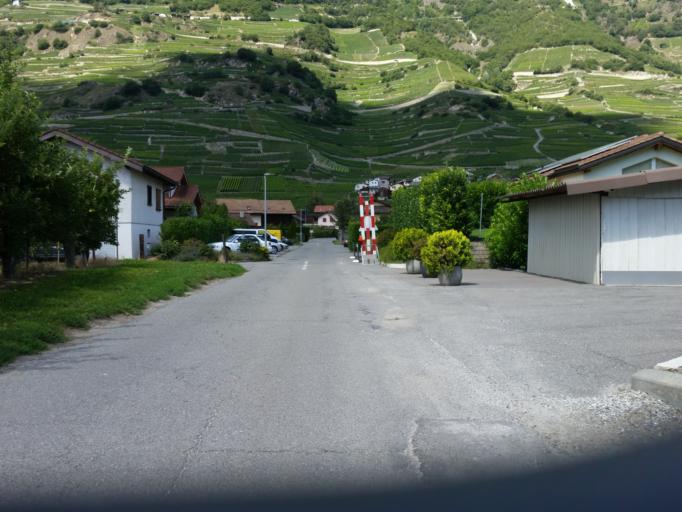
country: CH
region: Valais
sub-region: Martigny District
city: Fully
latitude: 46.1424
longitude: 7.1264
